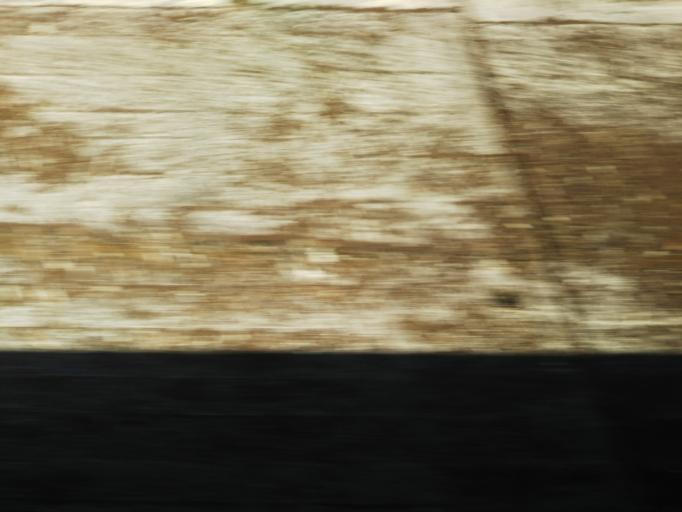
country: JP
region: Kochi
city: Nakamura
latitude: 33.0870
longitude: 133.1025
